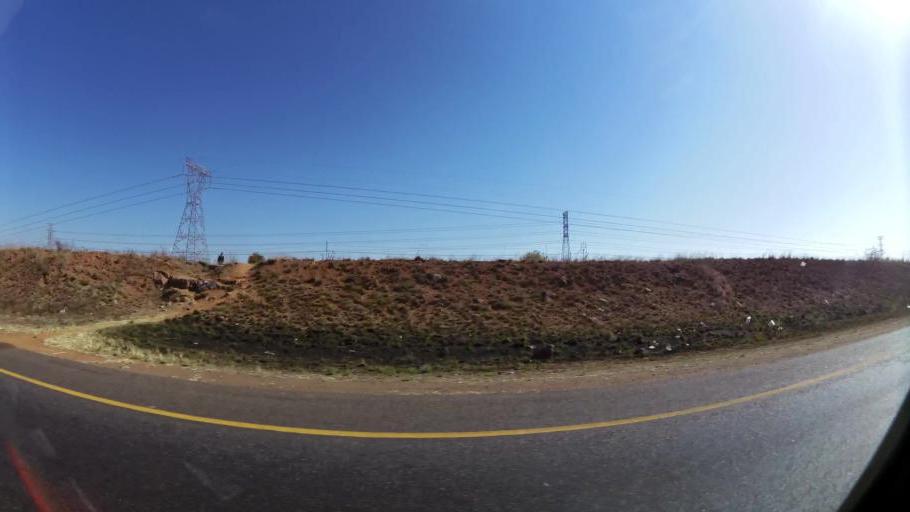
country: ZA
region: Gauteng
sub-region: City of Tshwane Metropolitan Municipality
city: Mabopane
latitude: -25.5448
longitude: 28.1111
